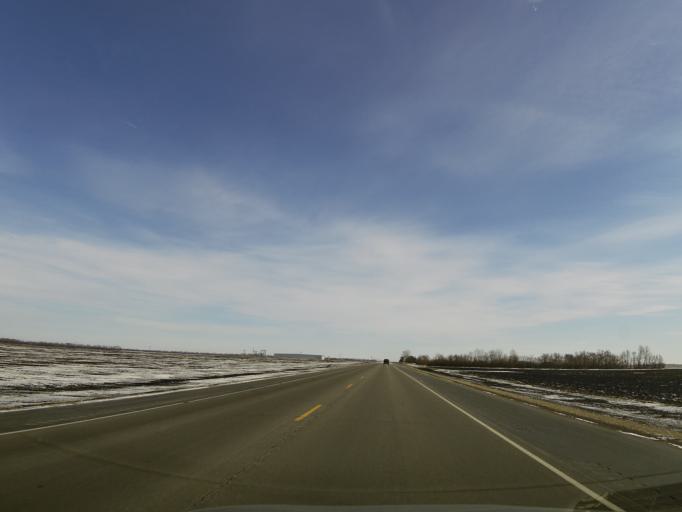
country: US
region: North Dakota
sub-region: Walsh County
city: Grafton
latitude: 48.4122
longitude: -97.3517
